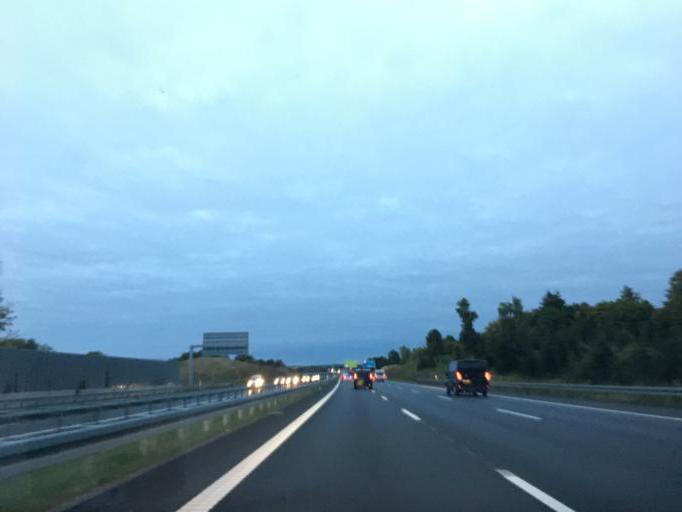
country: DK
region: Capital Region
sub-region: Horsholm Kommune
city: Horsholm
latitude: 55.8509
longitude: 12.5014
